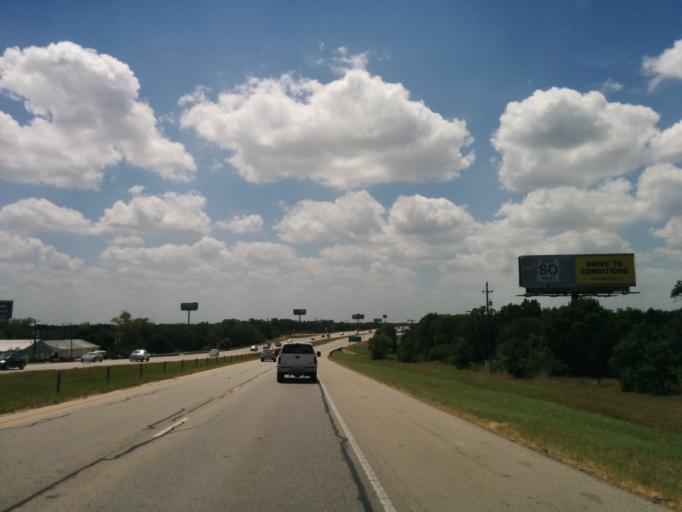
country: US
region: Texas
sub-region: Bastrop County
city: Wyldwood
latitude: 30.1108
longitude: -97.4069
